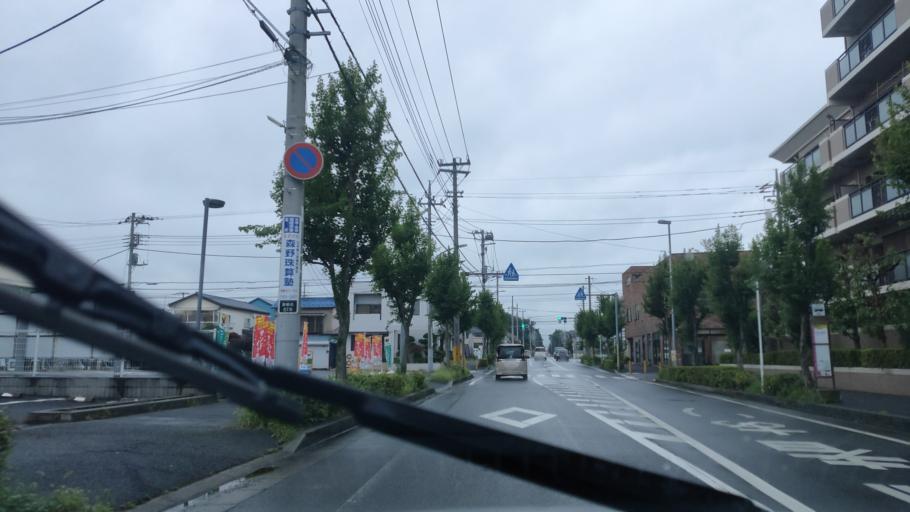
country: JP
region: Chiba
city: Nagareyama
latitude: 35.8834
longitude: 139.9137
